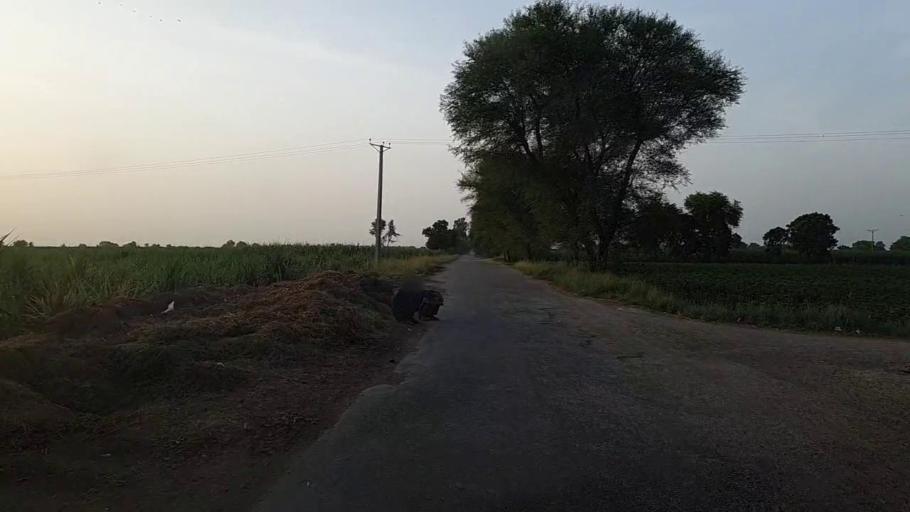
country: PK
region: Sindh
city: Ubauro
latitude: 28.2433
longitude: 69.8109
